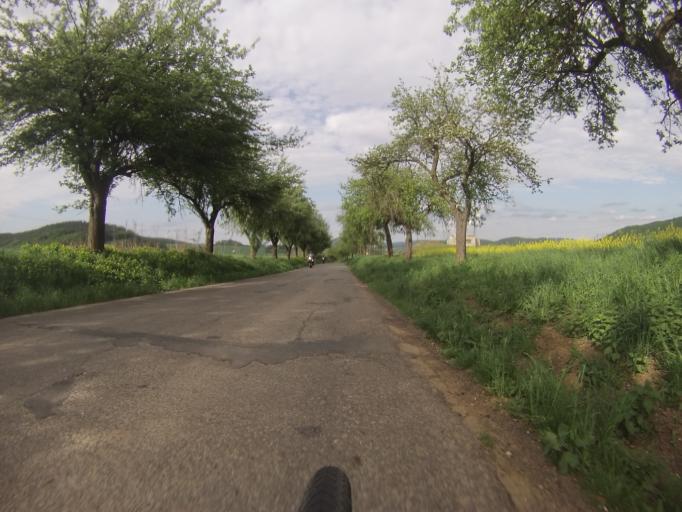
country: CZ
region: South Moravian
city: Veverska Bityska
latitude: 49.2890
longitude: 16.4470
